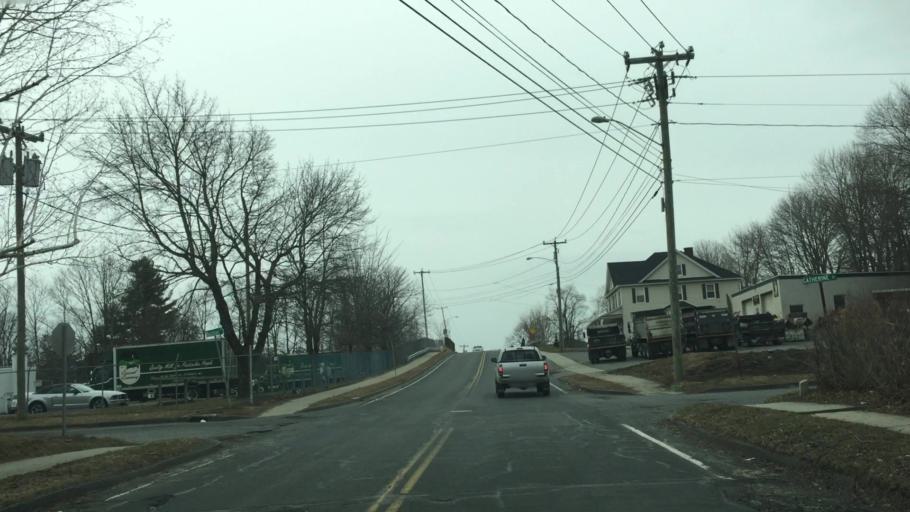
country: US
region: Massachusetts
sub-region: Berkshire County
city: Pittsfield
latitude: 42.4475
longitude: -73.2669
